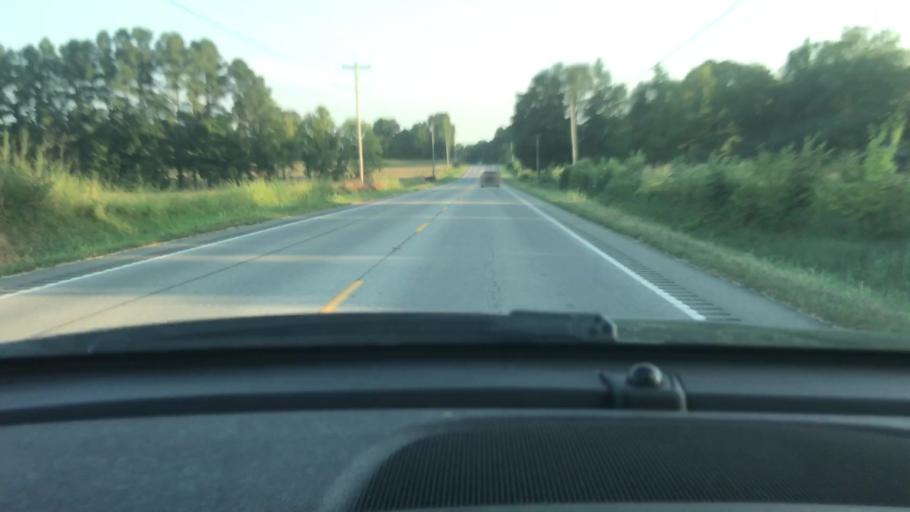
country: US
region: Tennessee
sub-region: Dickson County
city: Charlotte
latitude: 36.1451
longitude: -87.3569
